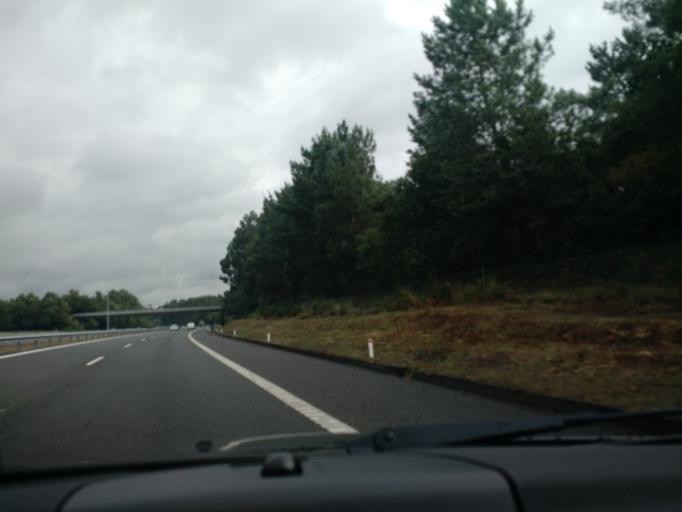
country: ES
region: Galicia
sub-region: Provincia da Coruna
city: Oroso
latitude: 42.9876
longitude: -8.4312
